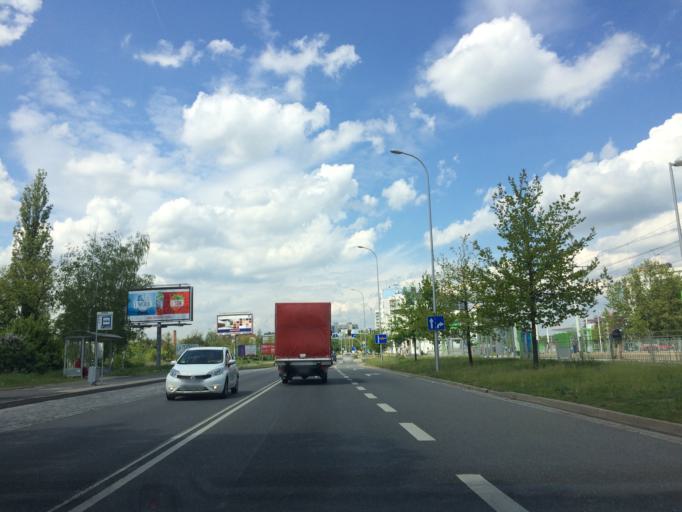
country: PL
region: Lower Silesian Voivodeship
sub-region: Powiat wroclawski
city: Wroclaw
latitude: 51.1361
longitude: 16.9672
